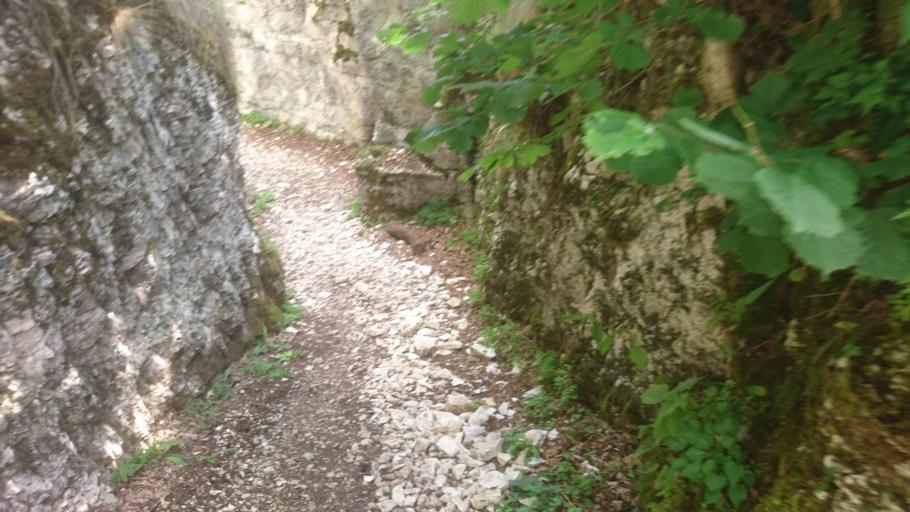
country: IT
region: Trentino-Alto Adige
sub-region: Provincia di Trento
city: Piazza
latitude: 45.8858
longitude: 11.1692
